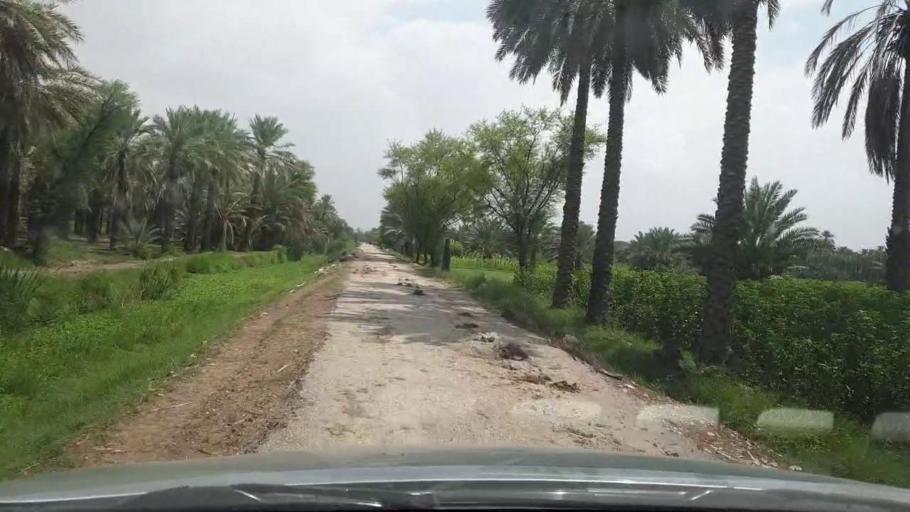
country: PK
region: Sindh
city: Kot Diji
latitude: 27.4141
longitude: 68.7597
